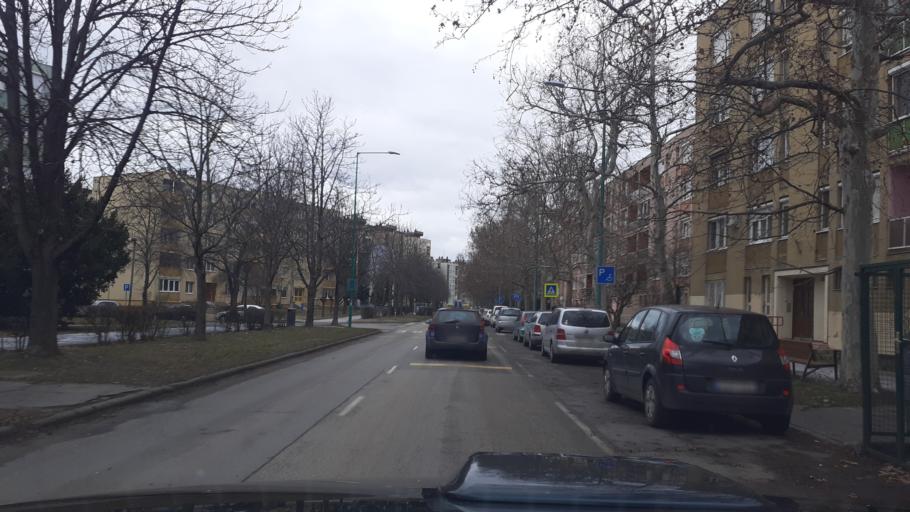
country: HU
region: Fejer
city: dunaujvaros
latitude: 46.9708
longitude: 18.9373
